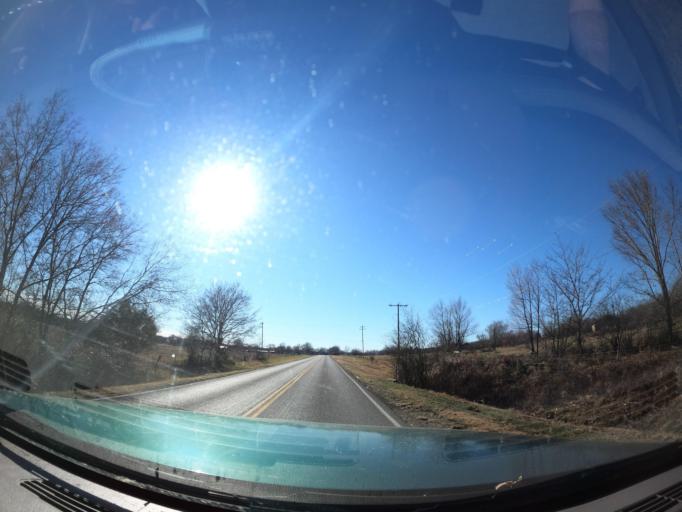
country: US
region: Oklahoma
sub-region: Muskogee County
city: Haskell
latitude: 35.6577
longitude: -95.6516
